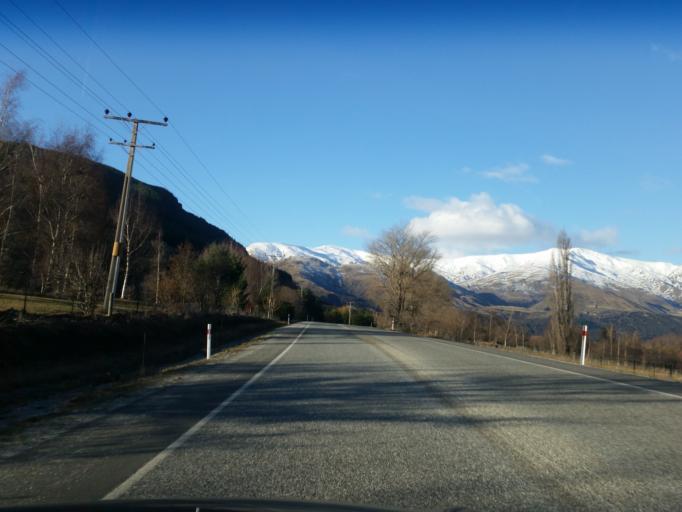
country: NZ
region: Otago
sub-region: Queenstown-Lakes District
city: Arrowtown
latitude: -44.9467
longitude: 168.7851
